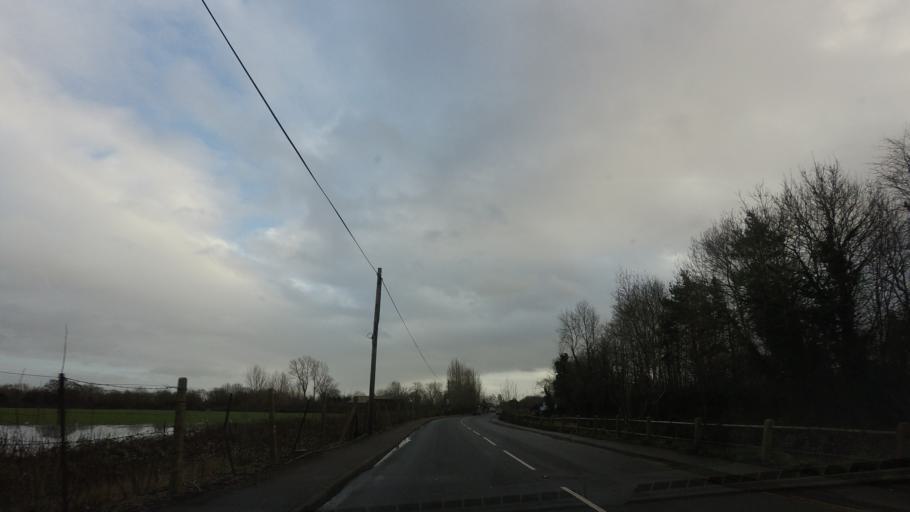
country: GB
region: England
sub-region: Kent
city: Yalding
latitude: 51.2246
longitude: 0.4184
